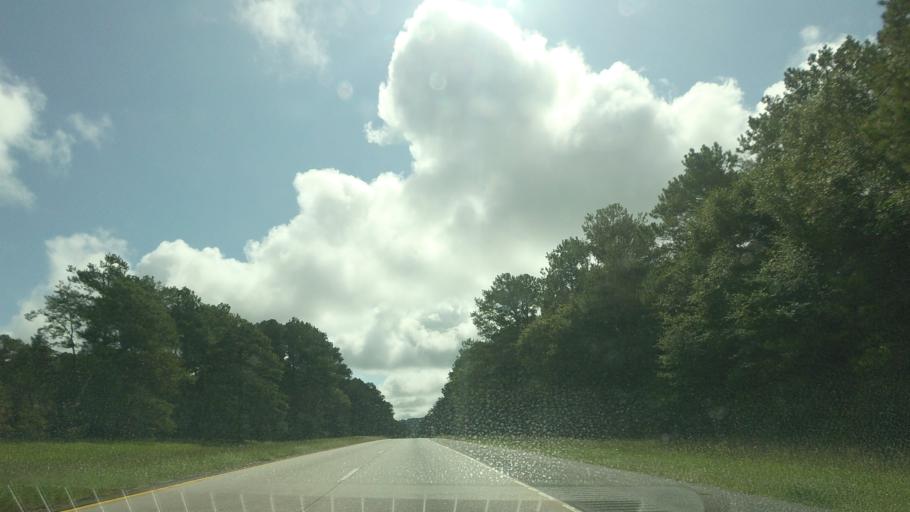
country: US
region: Georgia
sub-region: Twiggs County
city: Jeffersonville
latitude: 32.6510
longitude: -83.4289
